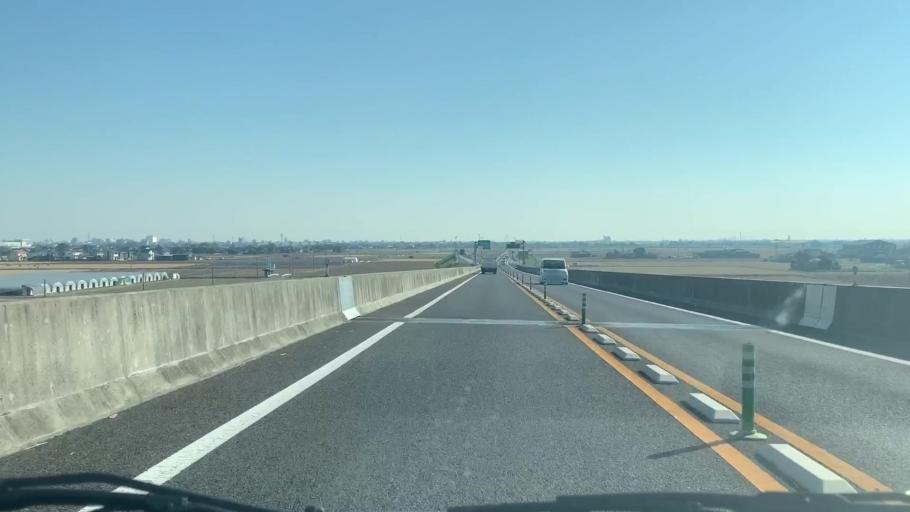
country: JP
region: Saga Prefecture
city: Saga-shi
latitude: 33.2316
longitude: 130.2507
